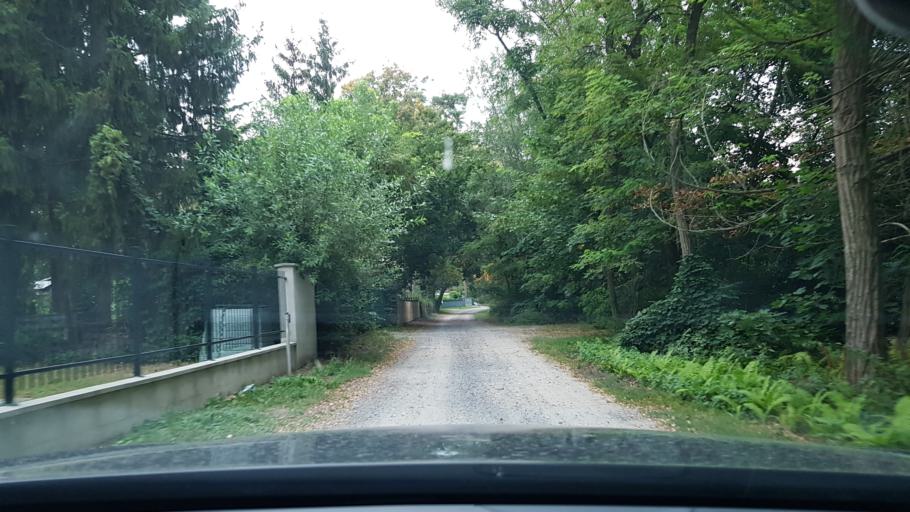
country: DE
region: Berlin
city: Mahlsdorf
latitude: 52.4827
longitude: 13.6298
